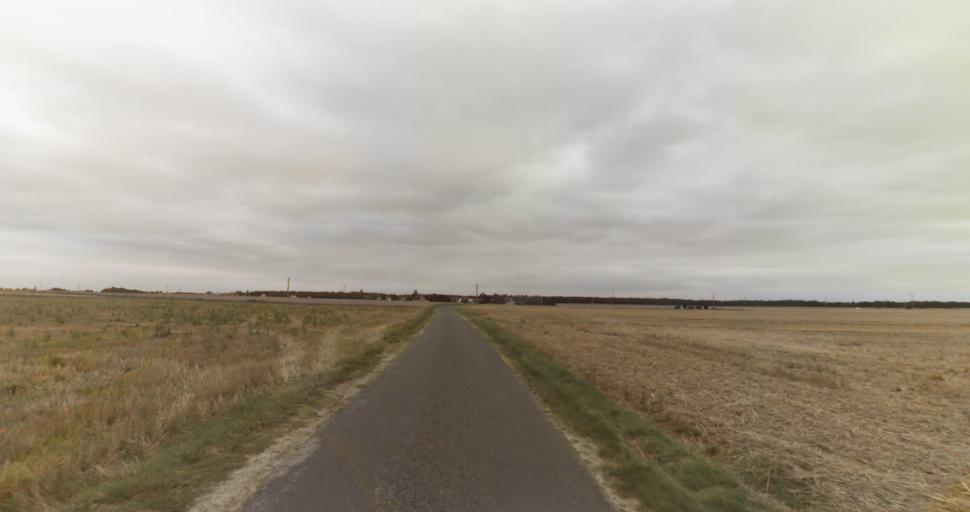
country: FR
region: Haute-Normandie
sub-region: Departement de l'Eure
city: La Couture-Boussey
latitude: 48.9186
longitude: 1.3921
